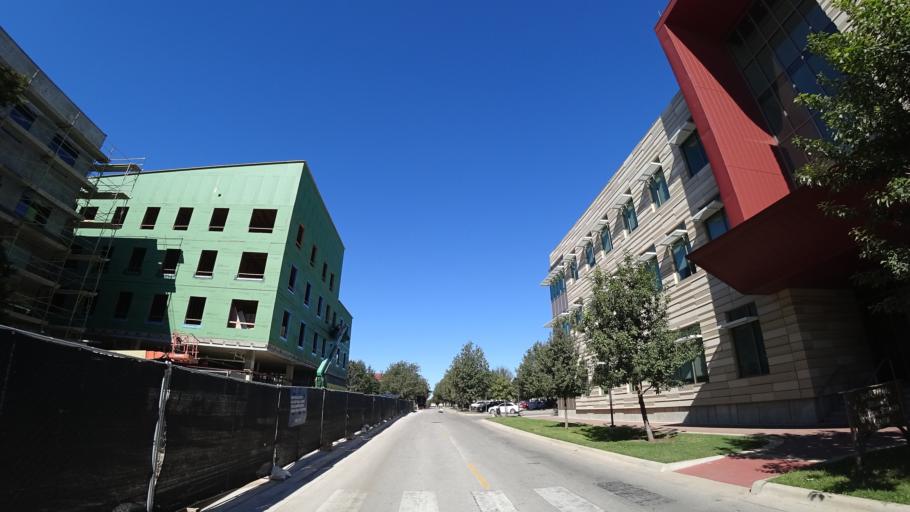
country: US
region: Texas
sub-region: Travis County
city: Austin
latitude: 30.2281
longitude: -97.7543
